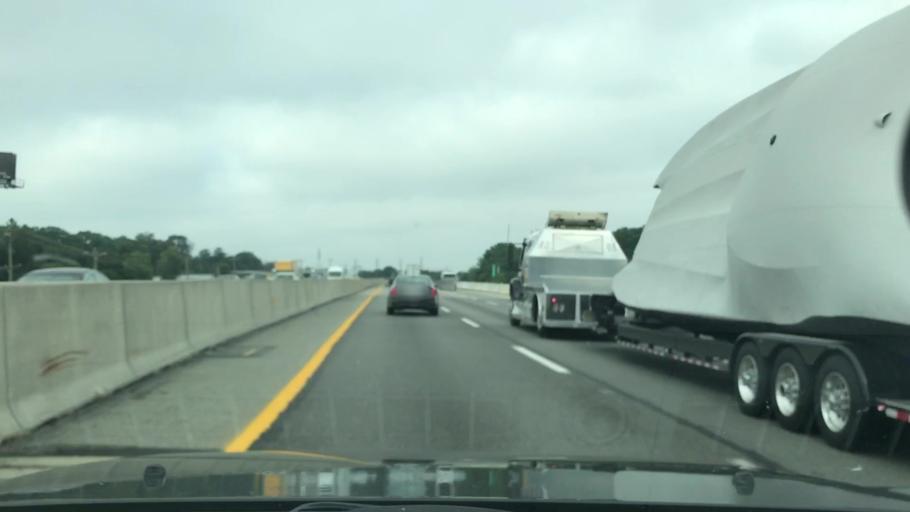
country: US
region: Pennsylvania
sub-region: Montgomery County
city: Bridgeport
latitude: 40.0878
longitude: -75.3568
